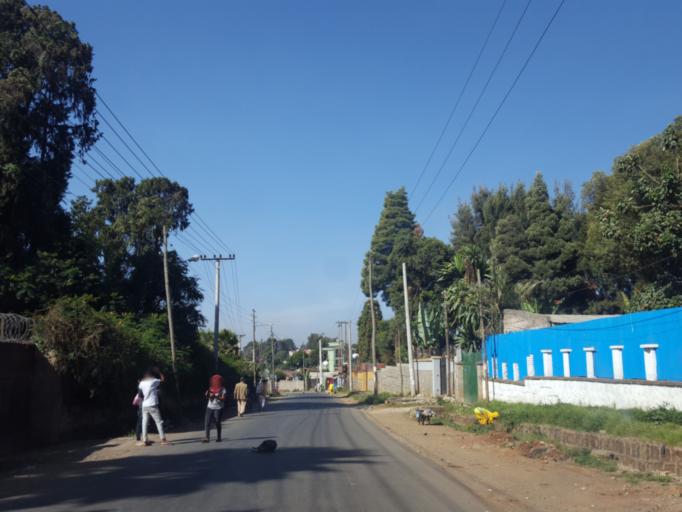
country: ET
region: Adis Abeba
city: Addis Ababa
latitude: 9.0529
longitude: 38.7408
